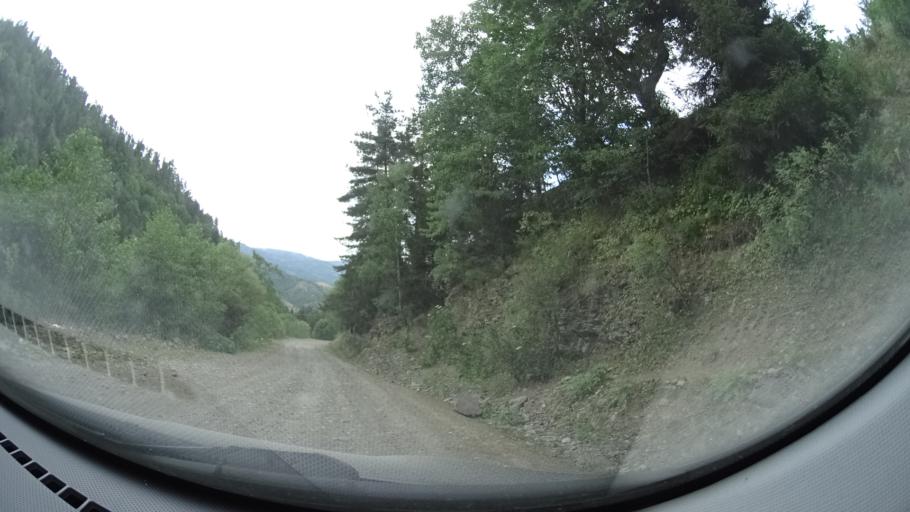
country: GE
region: Samtskhe-Javakheti
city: Adigeni
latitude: 41.6741
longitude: 42.6428
